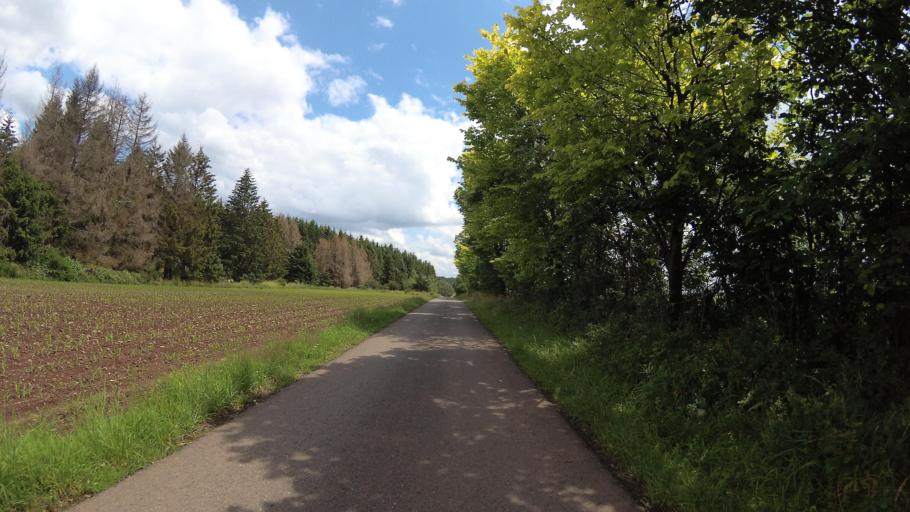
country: DE
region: Rheinland-Pfalz
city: Neuhutten
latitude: 49.5699
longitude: 7.0214
